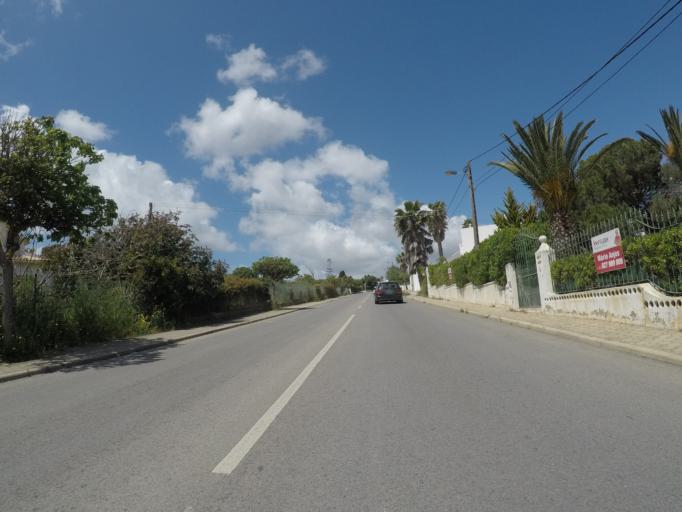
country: PT
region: Faro
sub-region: Silves
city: Armacao de Pera
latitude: 37.1036
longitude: -8.3719
